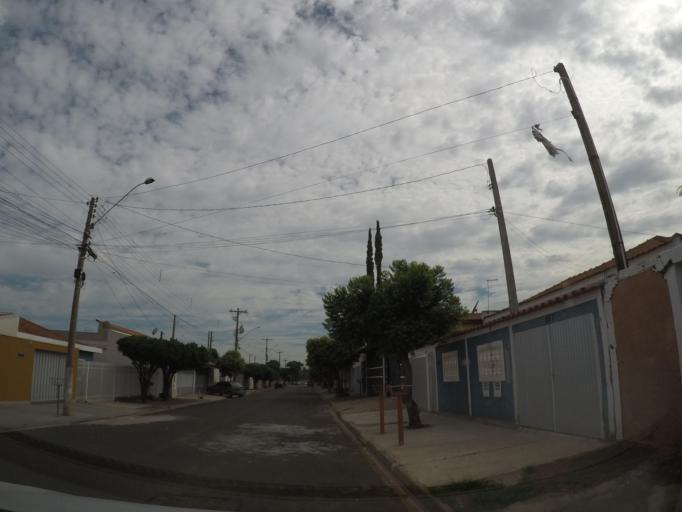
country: BR
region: Sao Paulo
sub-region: Hortolandia
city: Hortolandia
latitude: -22.8280
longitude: -47.1886
